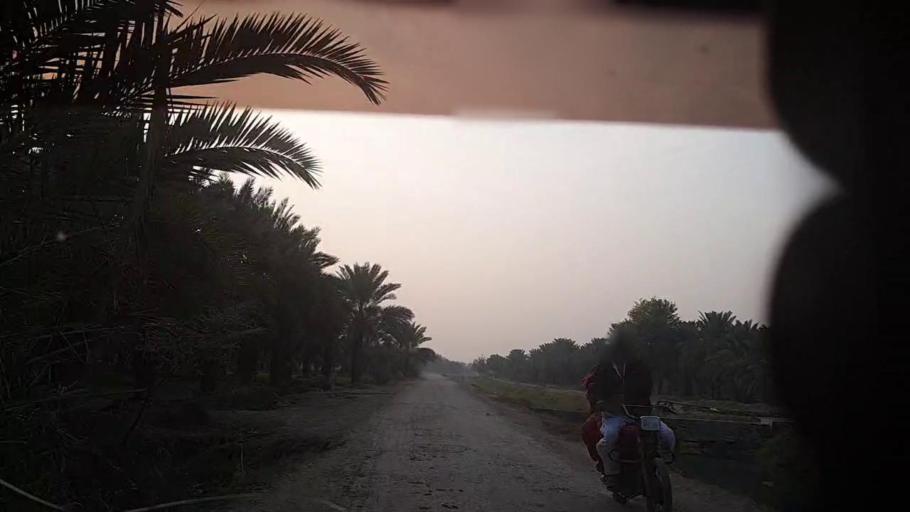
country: PK
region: Sindh
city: Pir jo Goth
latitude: 27.5213
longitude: 68.6489
